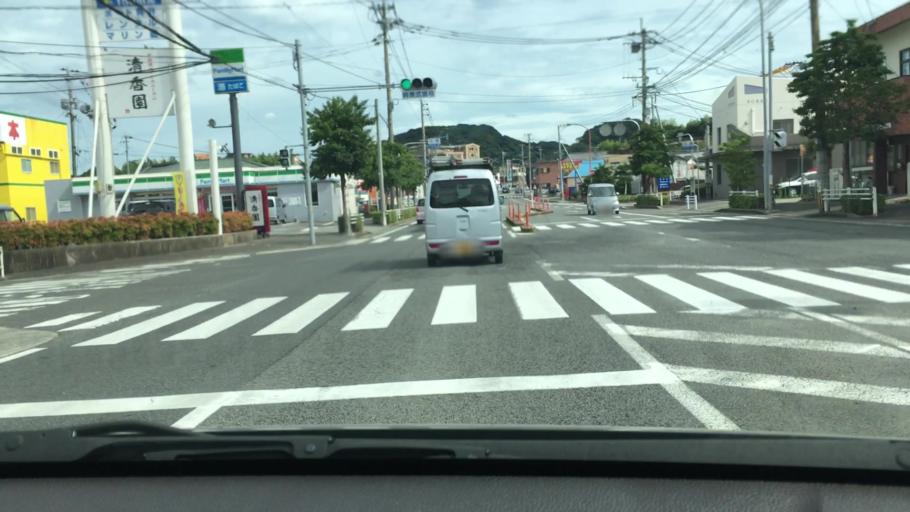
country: JP
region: Nagasaki
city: Togitsu
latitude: 32.8419
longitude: 129.8368
